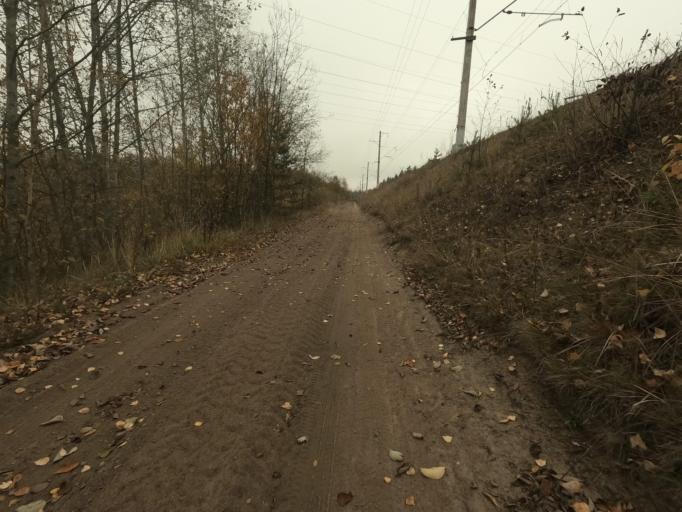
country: RU
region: Leningrad
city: Pavlovo
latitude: 59.7790
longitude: 30.8986
